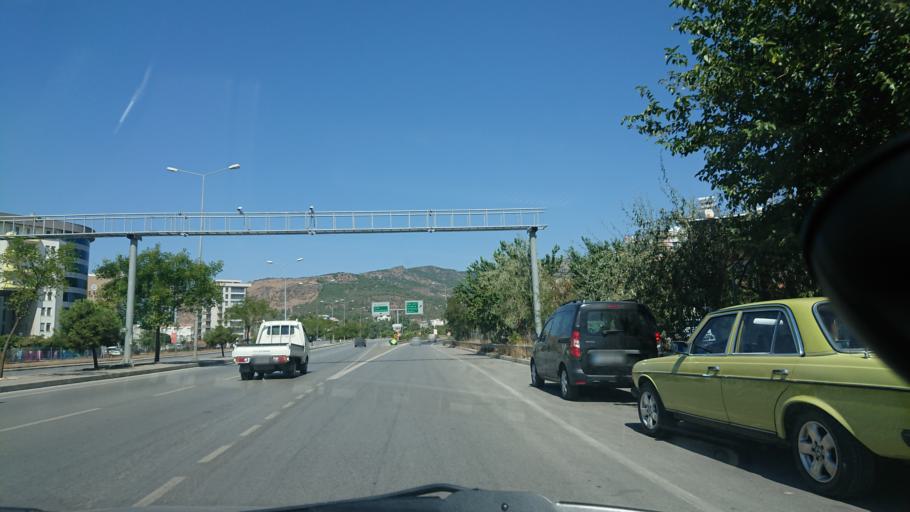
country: TR
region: Izmir
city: Karsiyaka
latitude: 38.4818
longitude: 27.1147
